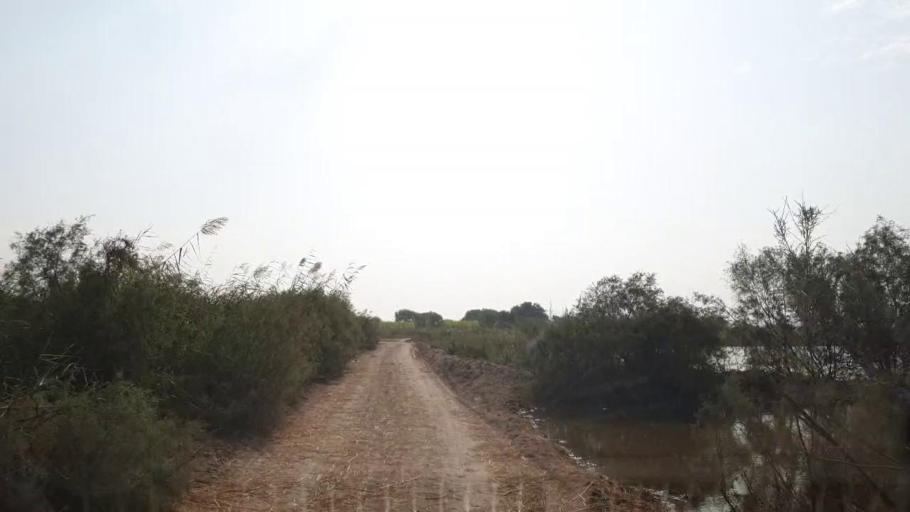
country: PK
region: Sindh
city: Tando Muhammad Khan
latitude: 25.0605
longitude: 68.4270
